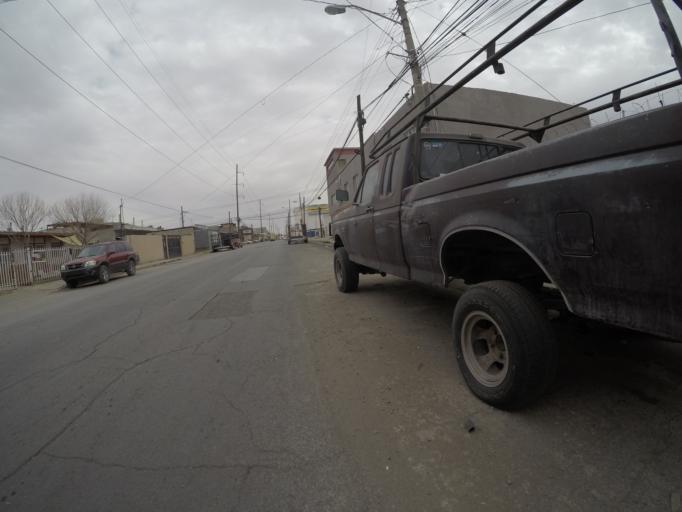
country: MX
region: Chihuahua
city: Ciudad Juarez
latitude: 31.7400
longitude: -106.4306
